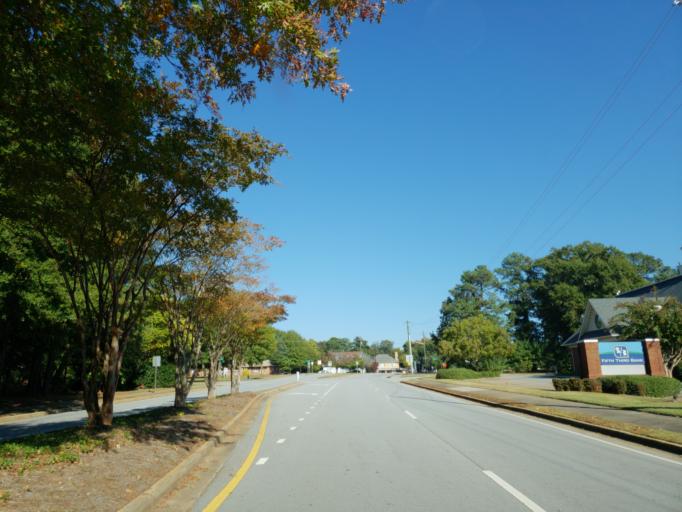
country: US
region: Georgia
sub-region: Gwinnett County
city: Lawrenceville
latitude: 33.9499
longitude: -83.9915
